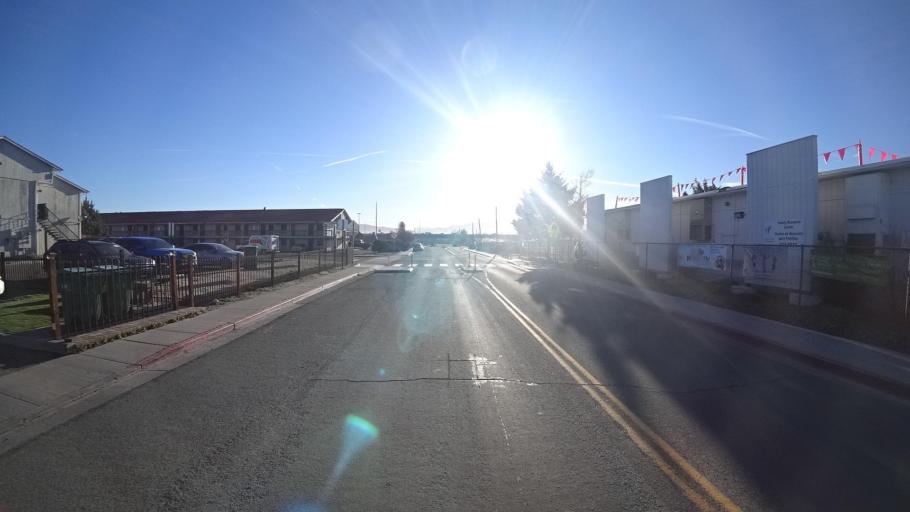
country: US
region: Nevada
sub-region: Washoe County
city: Reno
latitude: 39.5094
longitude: -119.7830
